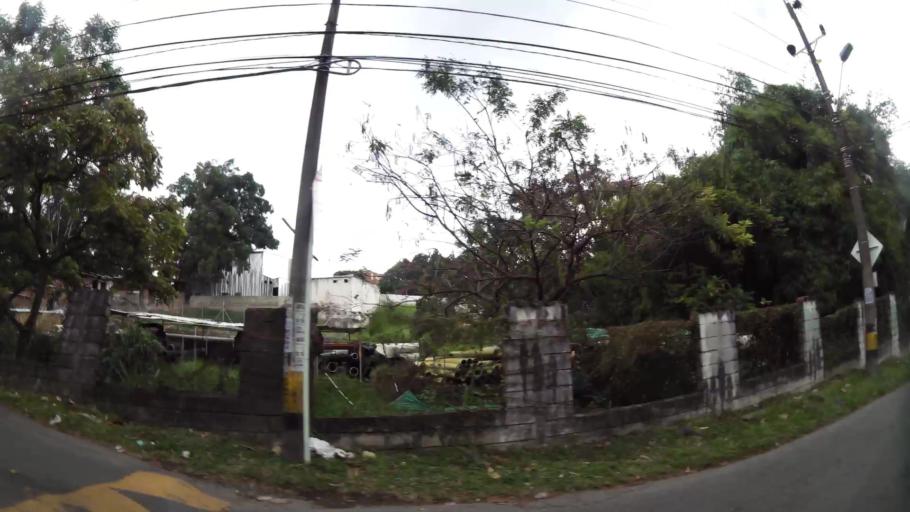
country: CO
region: Antioquia
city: Medellin
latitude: 6.2743
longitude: -75.5820
